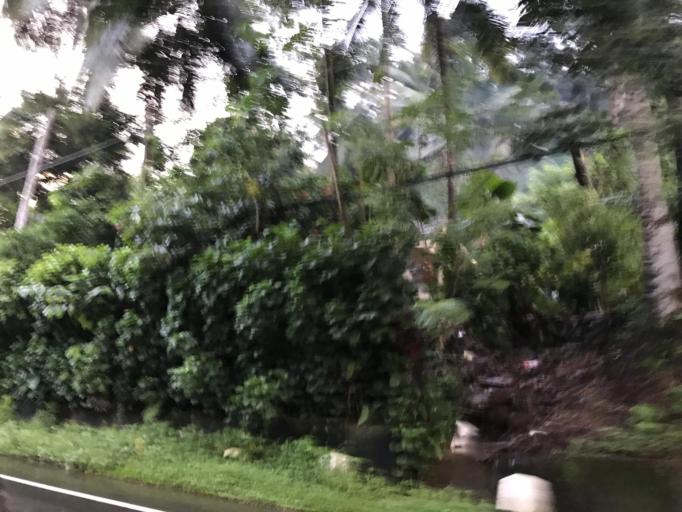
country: LK
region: Western
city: Horawala Junction
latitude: 6.5216
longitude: 80.2041
